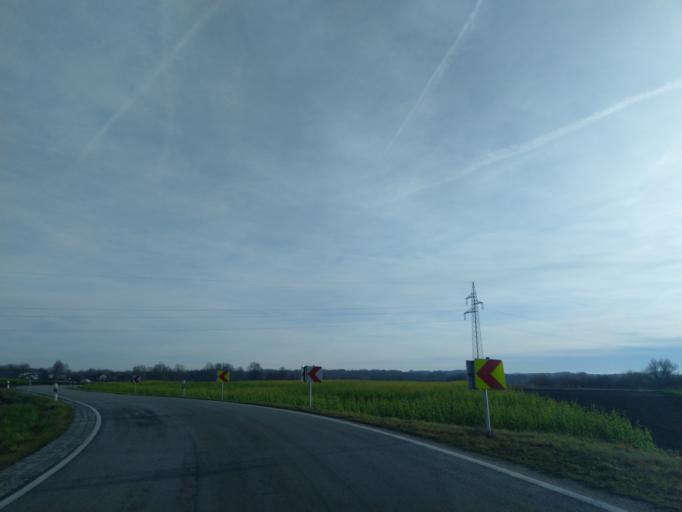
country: DE
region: Bavaria
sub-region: Lower Bavaria
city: Oberporing
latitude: 48.7169
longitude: 12.7984
